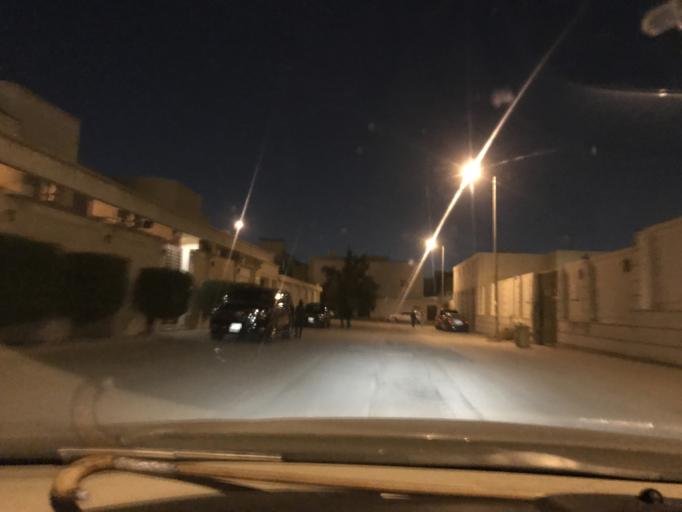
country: SA
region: Ar Riyad
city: Riyadh
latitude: 24.7559
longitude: 46.7529
